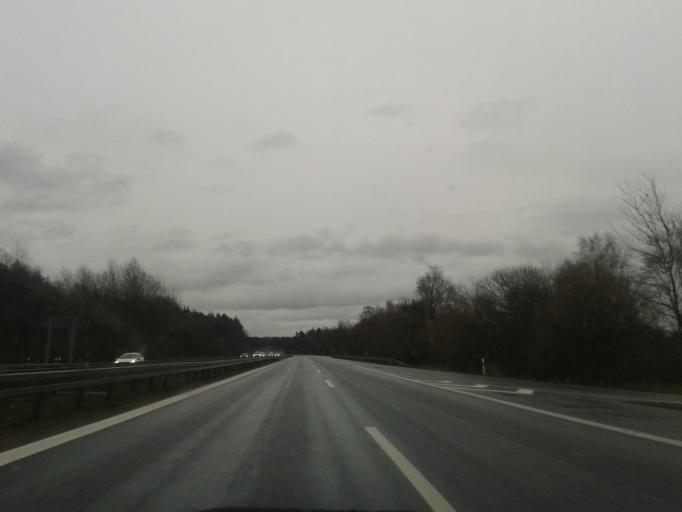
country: DE
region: Saxony
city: Lichtenberg
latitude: 51.1569
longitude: 13.9774
